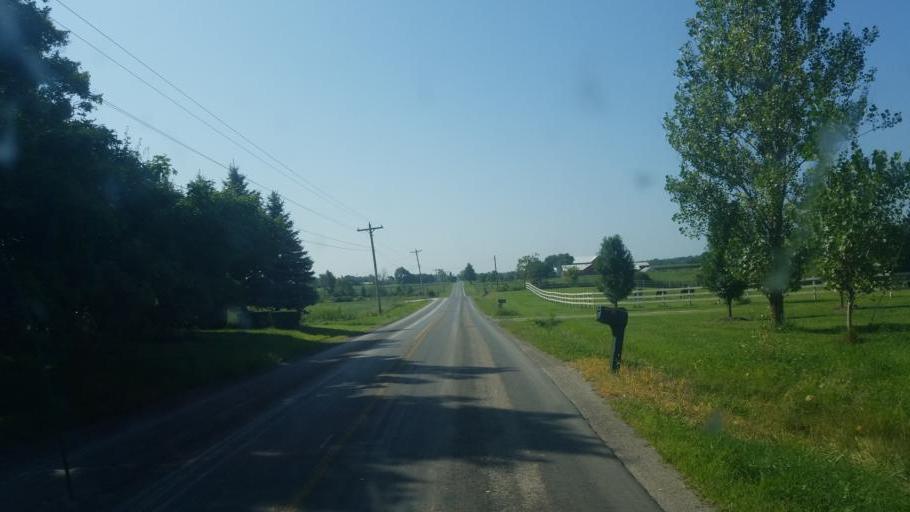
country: US
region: Ohio
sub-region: Wayne County
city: West Salem
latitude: 41.0084
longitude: -82.1640
